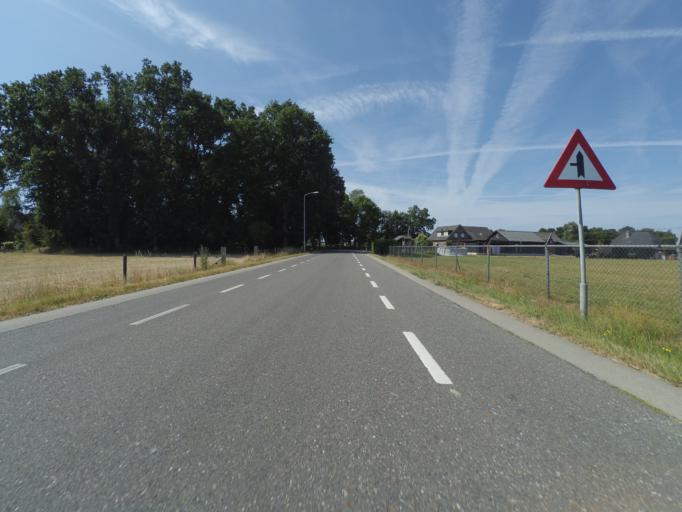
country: NL
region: Gelderland
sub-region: Gemeente Barneveld
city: Stroe
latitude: 52.1541
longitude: 5.7125
